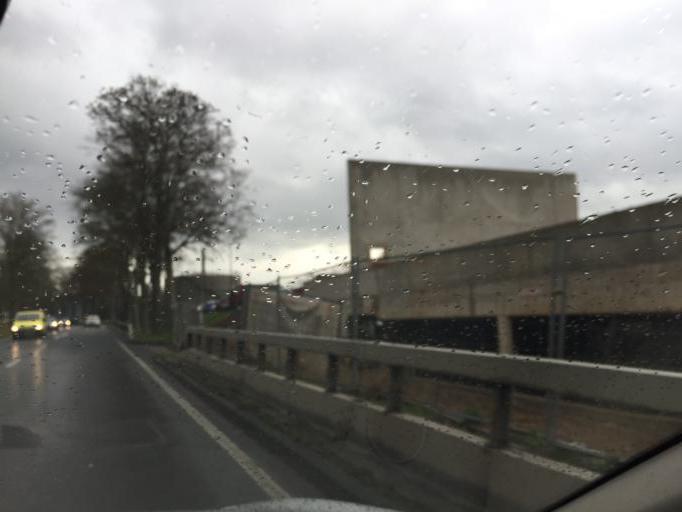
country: LU
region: Diekirch
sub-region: Canton de Vianden
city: Tandel
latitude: 49.8722
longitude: 6.1913
